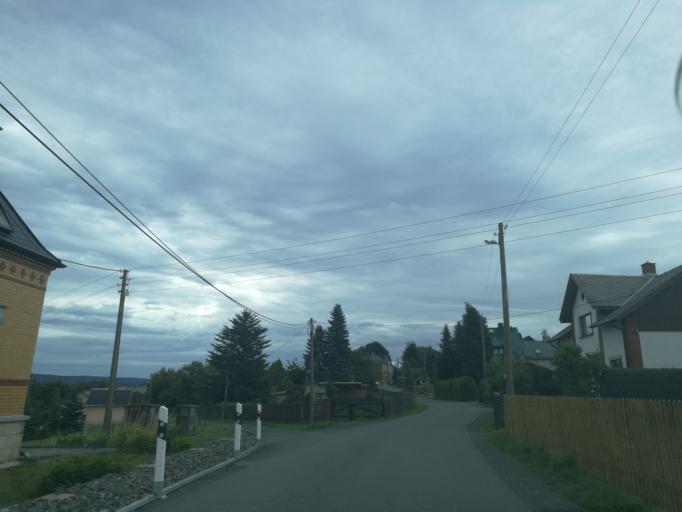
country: DE
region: Saxony
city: Adorf
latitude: 50.3106
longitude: 12.2747
